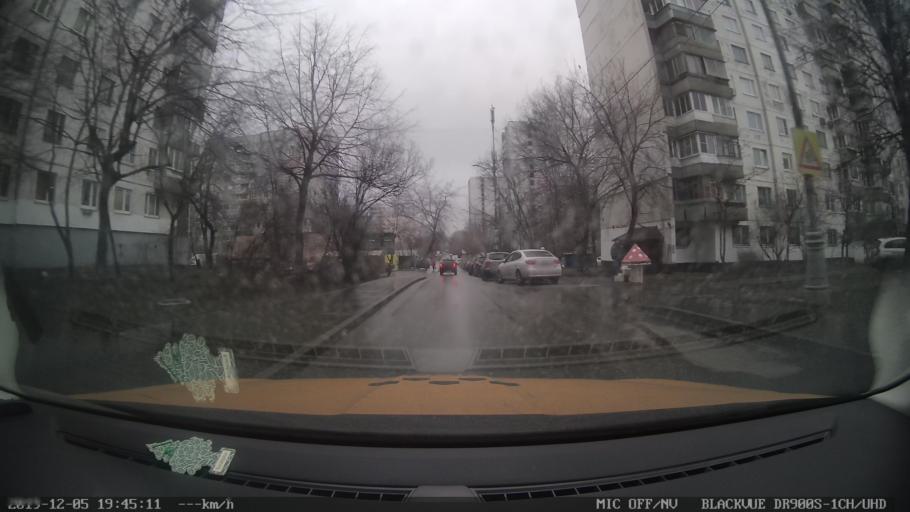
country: RU
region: Moscow
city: Lianozovo
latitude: 55.9022
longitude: 37.5769
